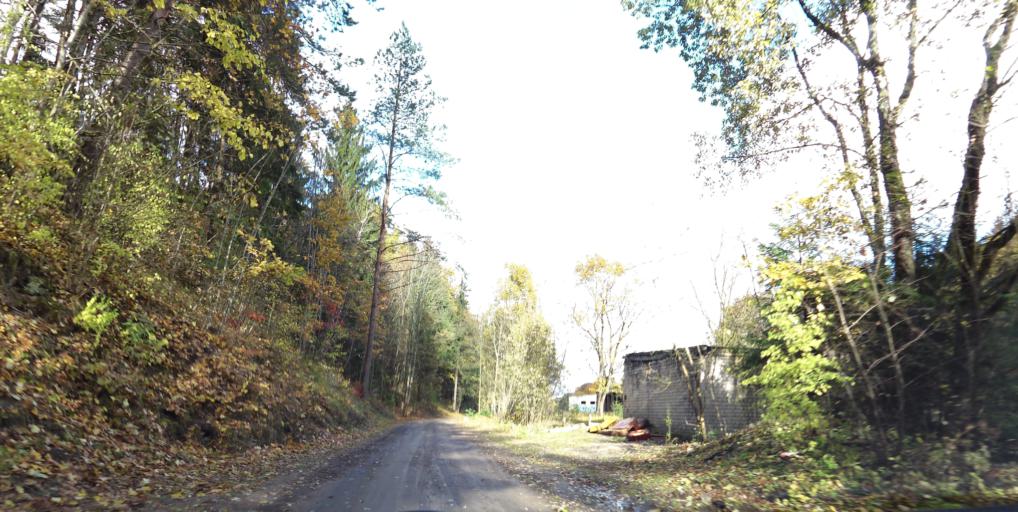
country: LT
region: Vilnius County
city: Vilkpede
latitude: 54.6554
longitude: 25.2576
